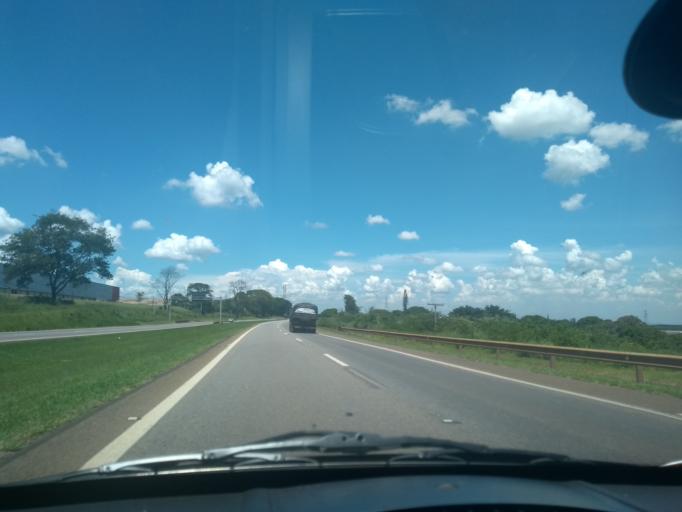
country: BR
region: Sao Paulo
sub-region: Mogi-Mirim
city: Mogi Mirim
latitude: -22.4857
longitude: -46.9812
